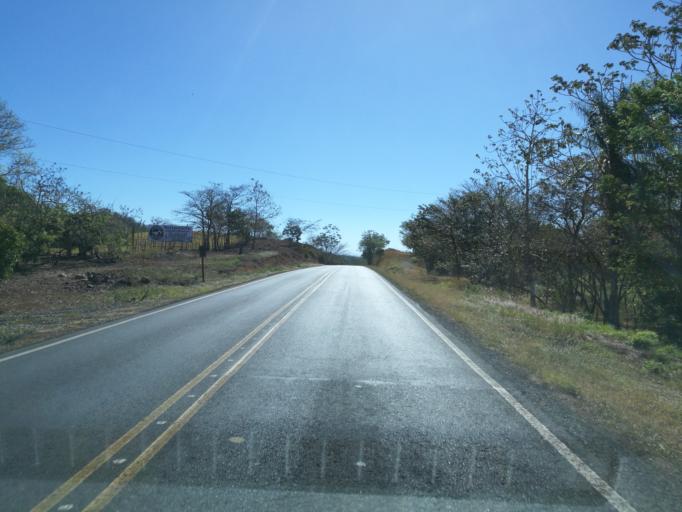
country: CR
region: Puntarenas
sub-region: Canton Central de Puntarenas
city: Puntarenas
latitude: 10.0992
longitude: -84.8664
